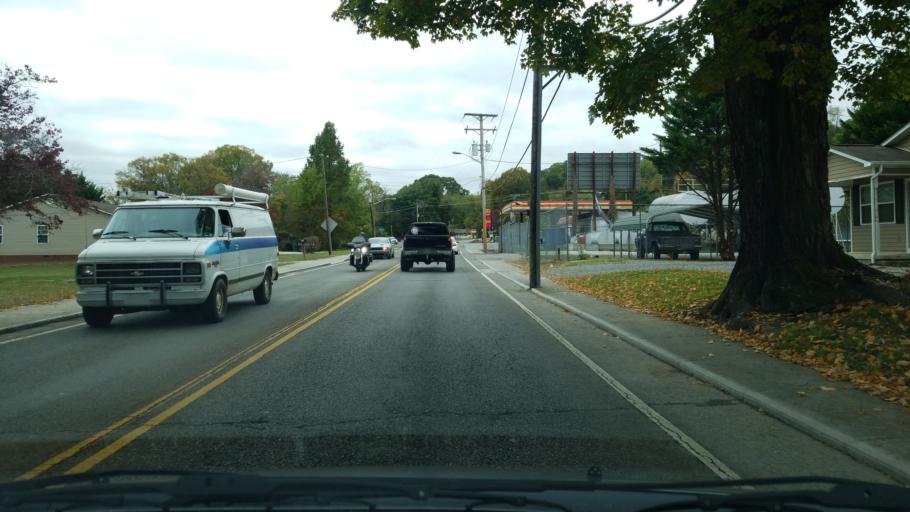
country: US
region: Tennessee
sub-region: Rhea County
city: Dayton
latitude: 35.4851
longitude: -85.0224
